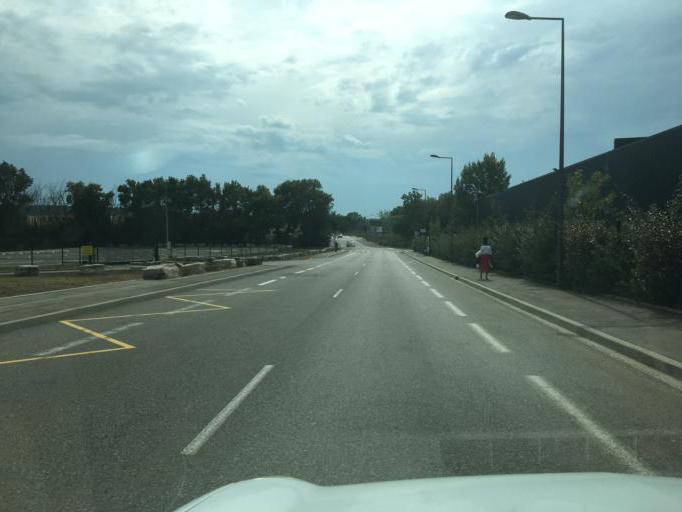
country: FR
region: Provence-Alpes-Cote d'Azur
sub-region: Departement des Bouches-du-Rhone
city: Bouc-Bel-Air
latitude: 43.4819
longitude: 5.3956
